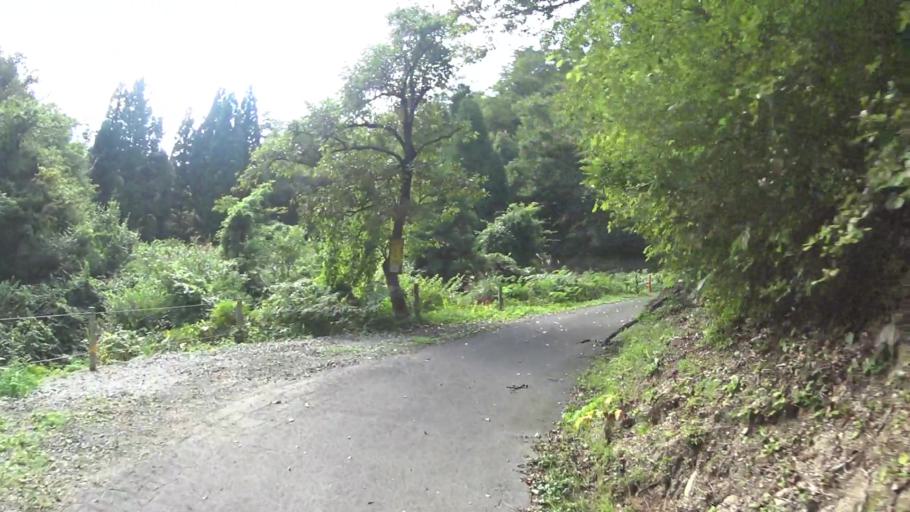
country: JP
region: Kyoto
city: Miyazu
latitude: 35.6722
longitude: 135.1439
